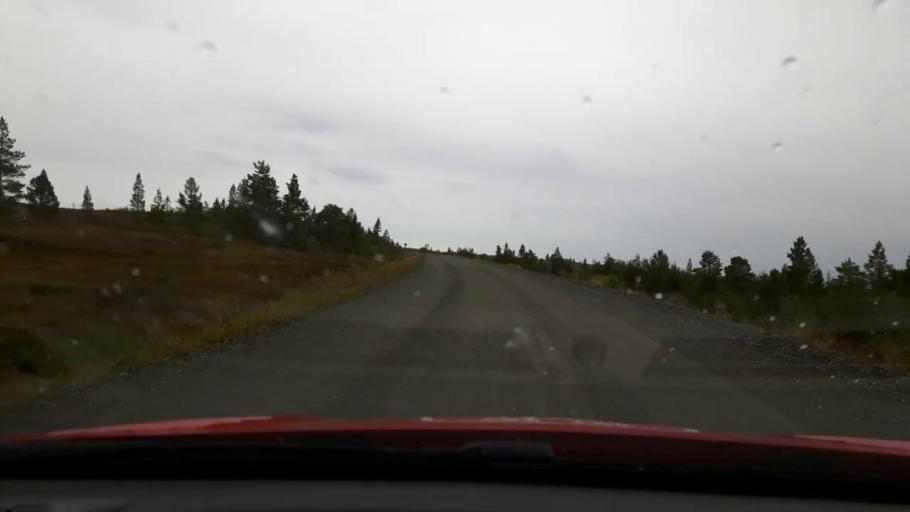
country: NO
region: Nord-Trondelag
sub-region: Meraker
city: Meraker
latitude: 63.6340
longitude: 12.2800
